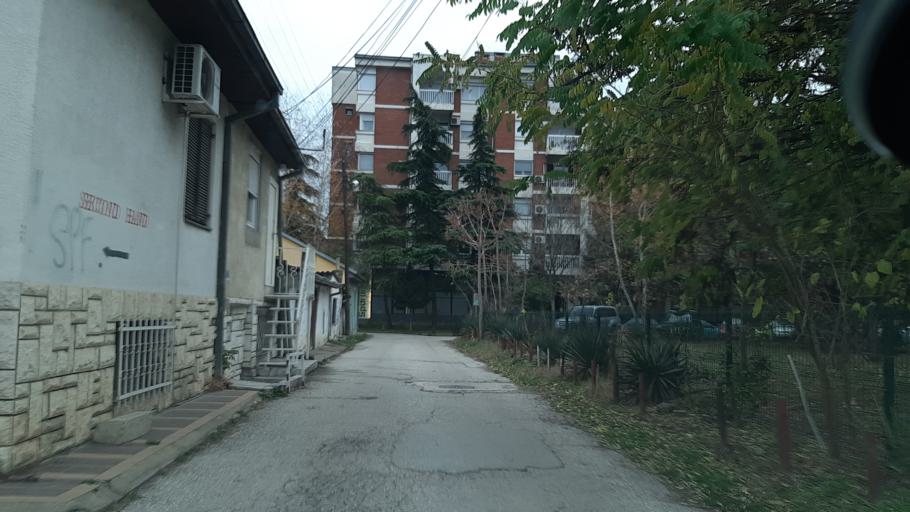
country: MK
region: Karpos
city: Skopje
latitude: 41.9917
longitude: 21.4397
